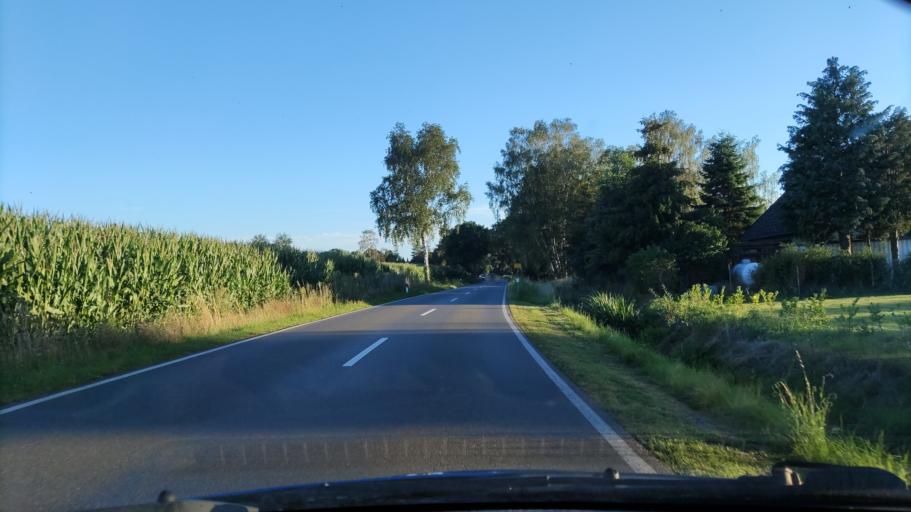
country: DE
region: Lower Saxony
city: Luechow
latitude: 53.0040
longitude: 11.1533
